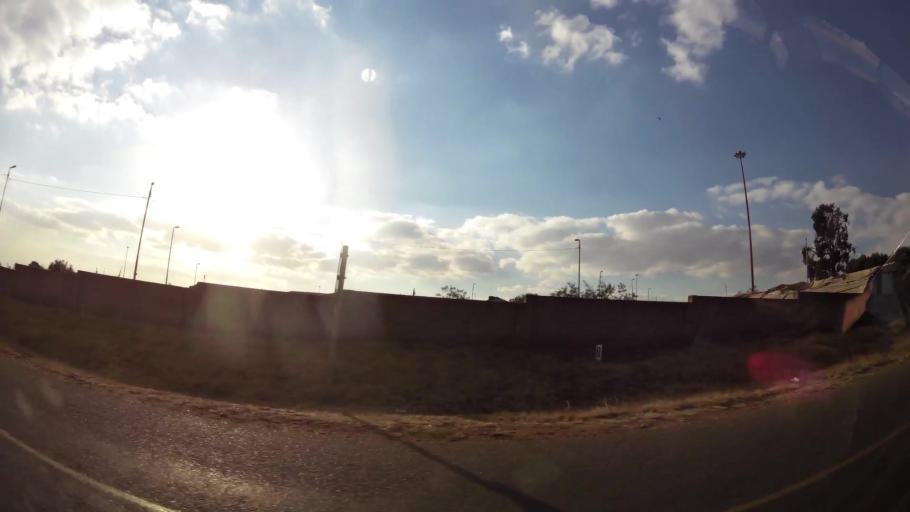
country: ZA
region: Gauteng
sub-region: West Rand District Municipality
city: Krugersdorp
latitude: -26.0822
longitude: 27.7572
